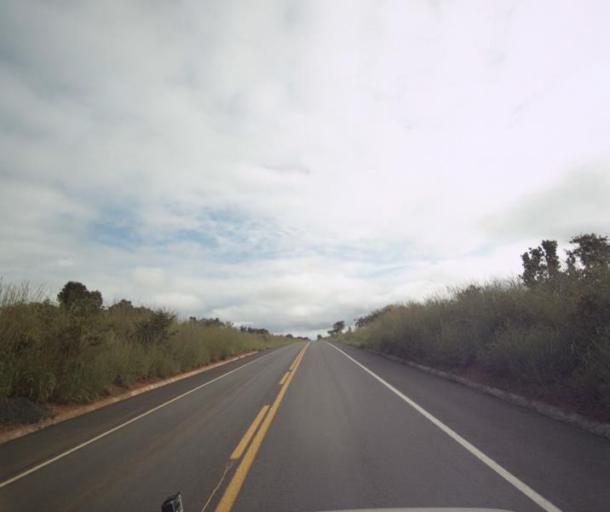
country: BR
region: Goias
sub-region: Padre Bernardo
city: Padre Bernardo
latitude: -15.3655
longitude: -48.6460
